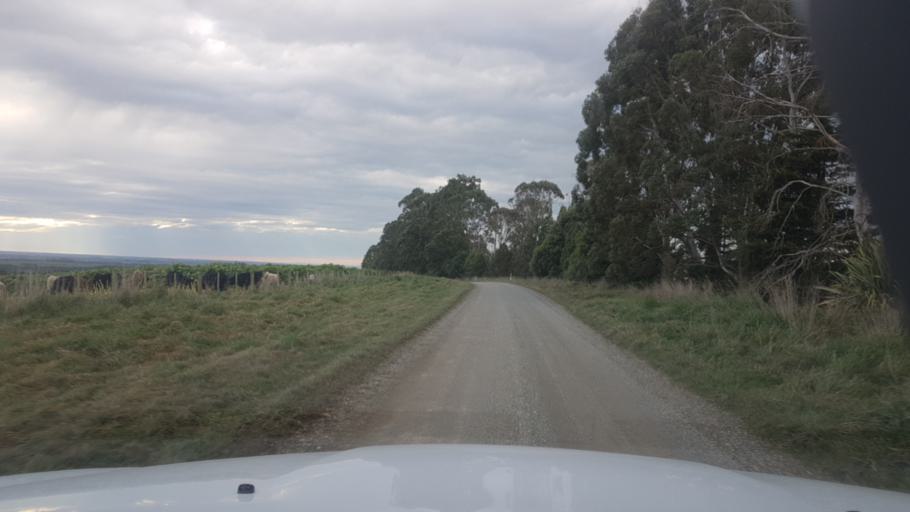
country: NZ
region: Canterbury
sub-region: Timaru District
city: Pleasant Point
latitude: -44.3456
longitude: 171.1335
